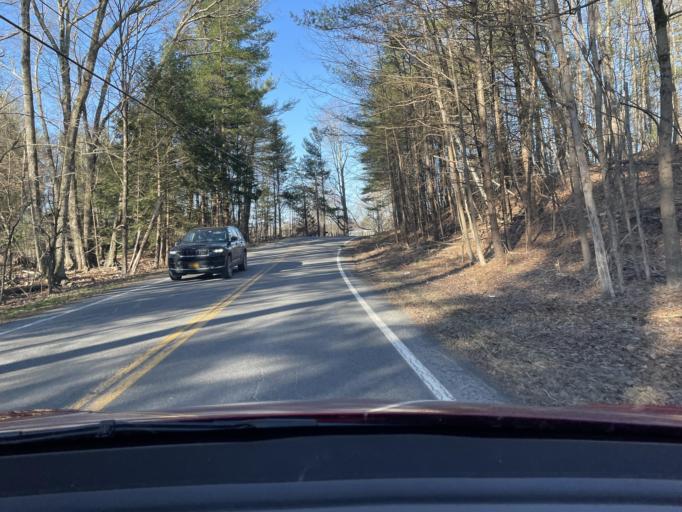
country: US
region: New York
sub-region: Ulster County
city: Zena
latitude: 42.0463
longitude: -74.0407
